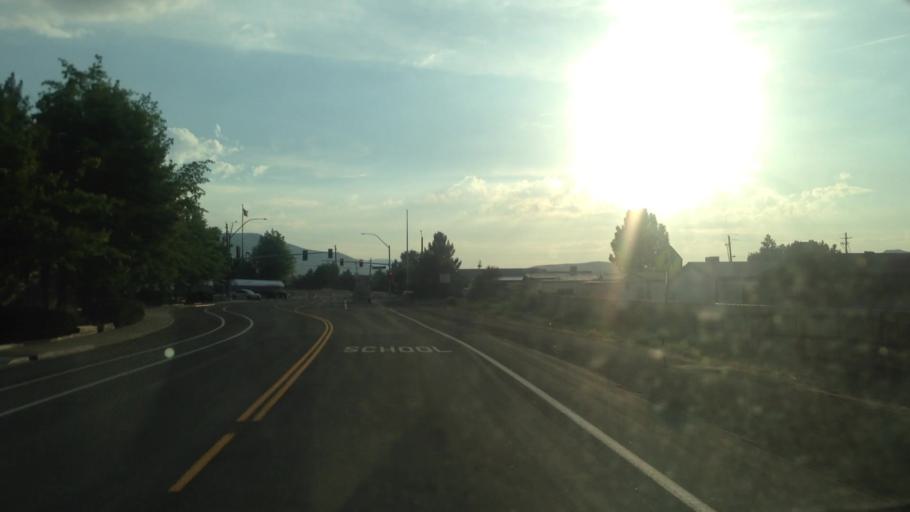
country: US
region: Nevada
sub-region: Washoe County
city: Lemmon Valley
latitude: 39.6255
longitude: -119.8803
